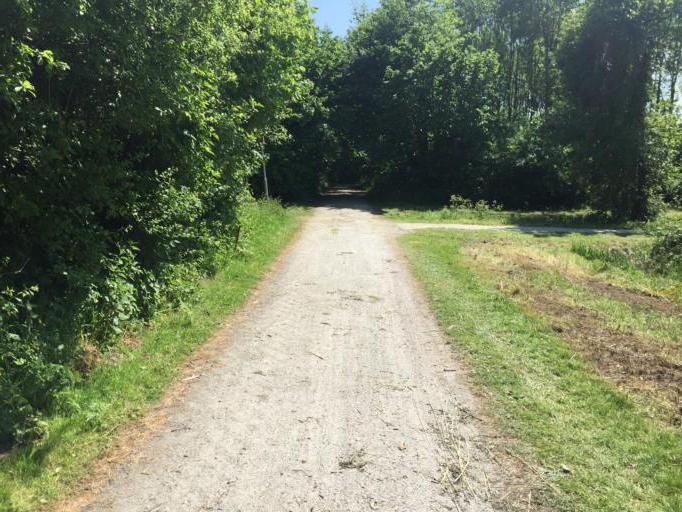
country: NL
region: Groningen
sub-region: Gemeente Zuidhorn
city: Grijpskerk
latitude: 53.2171
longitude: 6.3368
